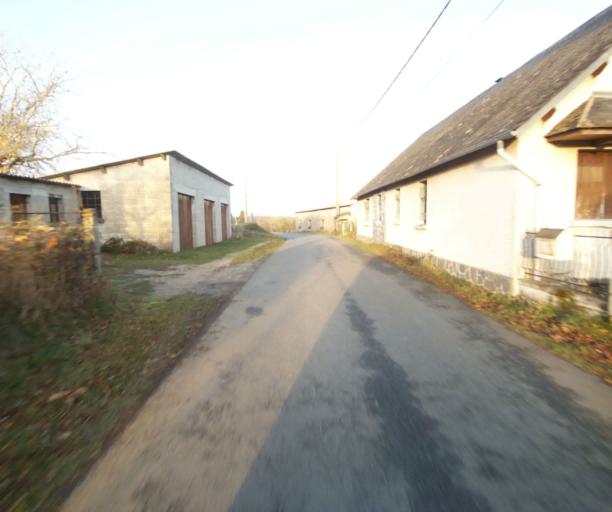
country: FR
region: Limousin
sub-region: Departement de la Correze
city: Laguenne
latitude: 45.2306
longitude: 1.8253
